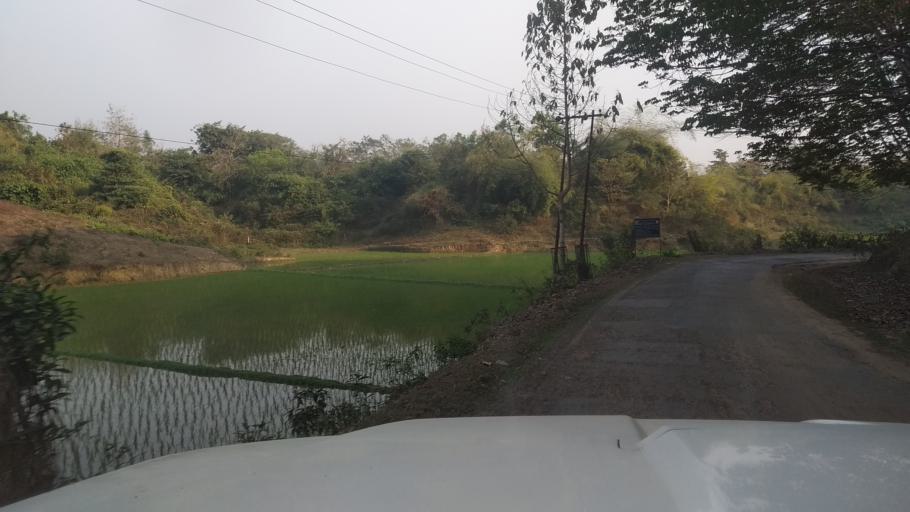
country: IN
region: Tripura
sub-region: West Tripura
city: Sonamura
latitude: 23.3443
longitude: 91.3208
